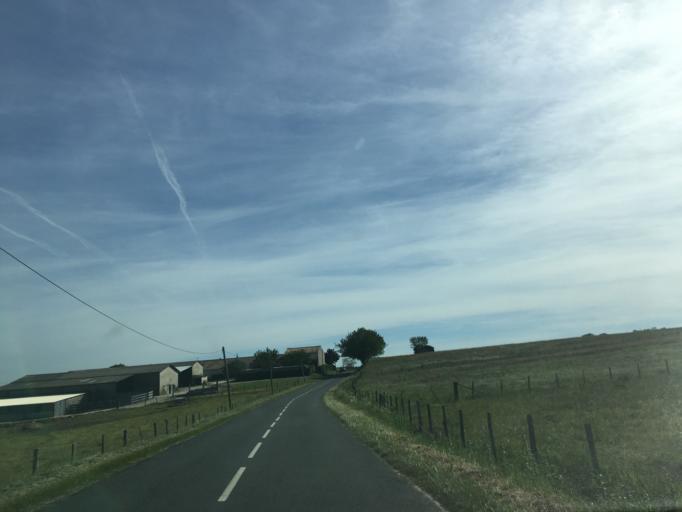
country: FR
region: Poitou-Charentes
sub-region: Departement de la Charente-Maritime
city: Mirambeau
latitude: 45.3404
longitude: -0.5882
